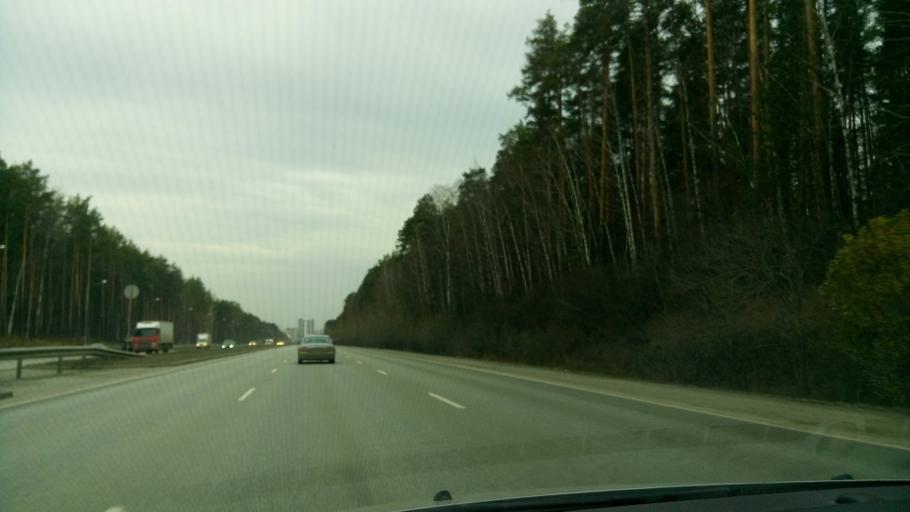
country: RU
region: Sverdlovsk
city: Istok
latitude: 56.8161
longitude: 60.7366
